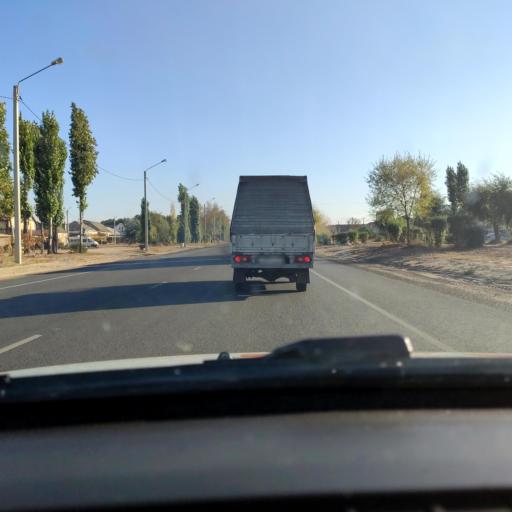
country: RU
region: Voronezj
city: Pridonskoy
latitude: 51.7031
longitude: 39.0767
